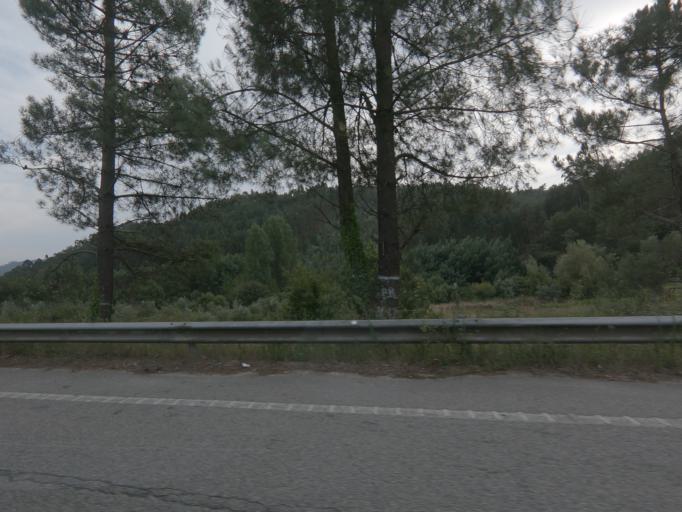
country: PT
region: Coimbra
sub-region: Penacova
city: Lorvao
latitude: 40.3017
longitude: -8.3166
